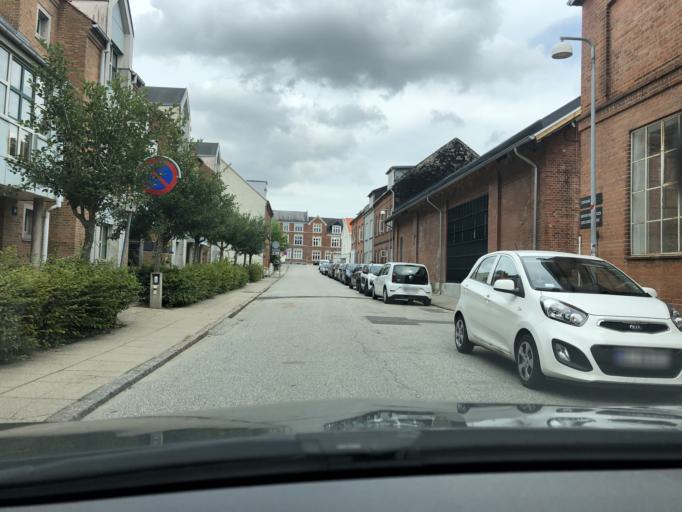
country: DK
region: South Denmark
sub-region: Vejle Kommune
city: Vejle
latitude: 55.7144
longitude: 9.5308
